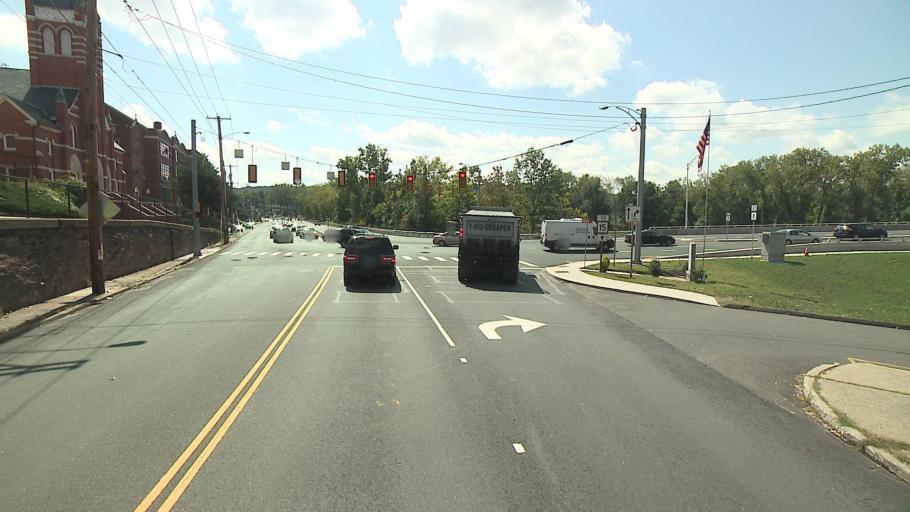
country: US
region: Connecticut
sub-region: New Haven County
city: Derby
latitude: 41.3190
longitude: -73.0810
